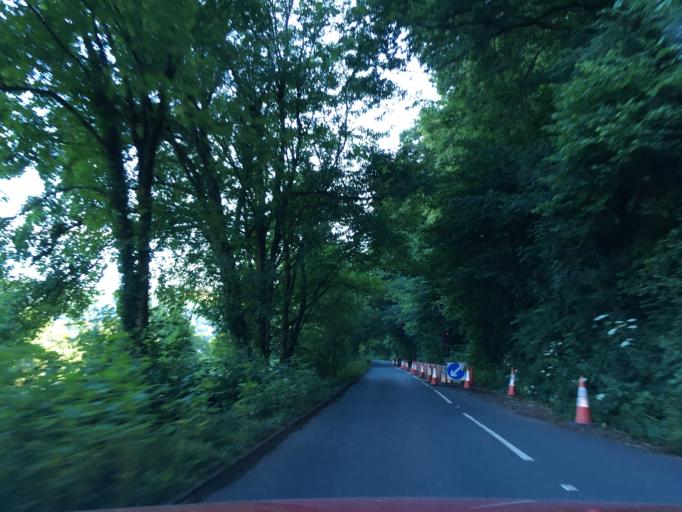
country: GB
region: Wales
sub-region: Monmouthshire
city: Tintern
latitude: 51.7482
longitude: -2.6649
